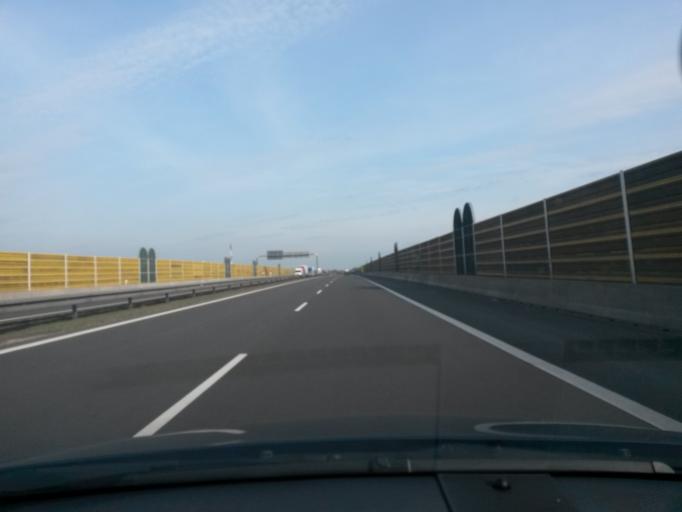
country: PL
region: Greater Poland Voivodeship
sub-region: Powiat wrzesinski
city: Wrzesnia
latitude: 52.3130
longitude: 17.5464
